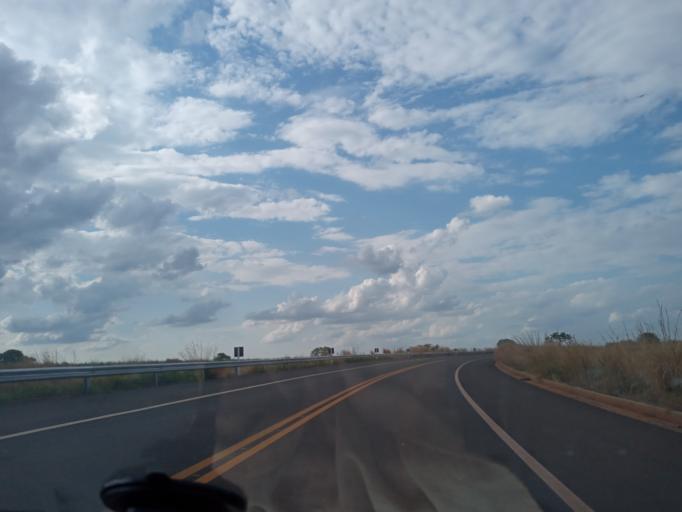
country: BR
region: Minas Gerais
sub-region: Ituiutaba
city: Ituiutaba
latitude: -19.1565
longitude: -49.5278
